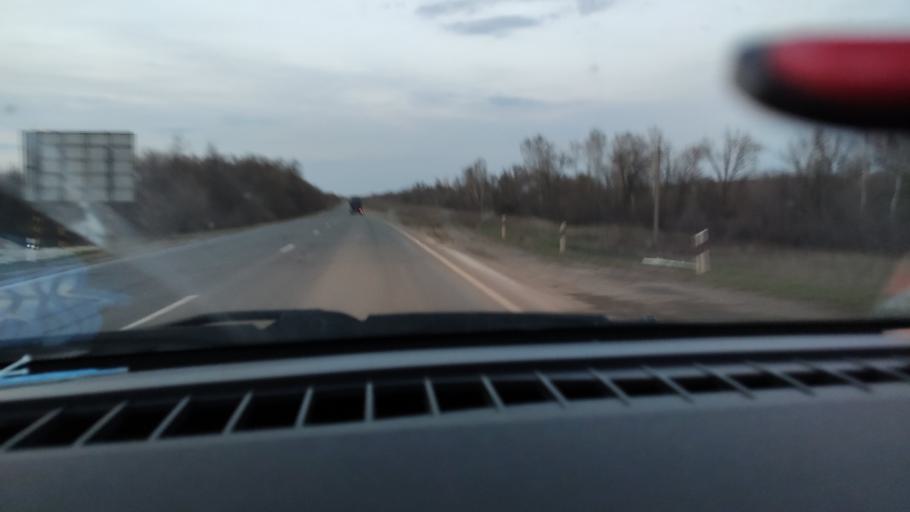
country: RU
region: Saratov
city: Sinodskoye
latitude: 52.0301
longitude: 46.7210
